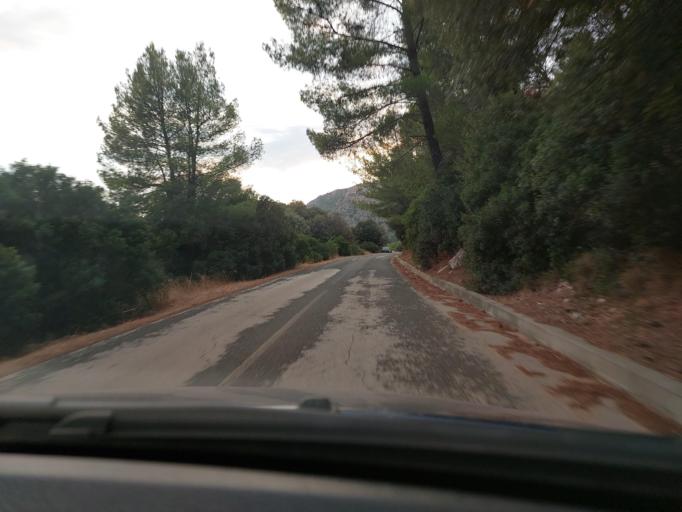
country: HR
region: Dubrovacko-Neretvanska
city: Smokvica
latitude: 42.7609
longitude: 16.9002
